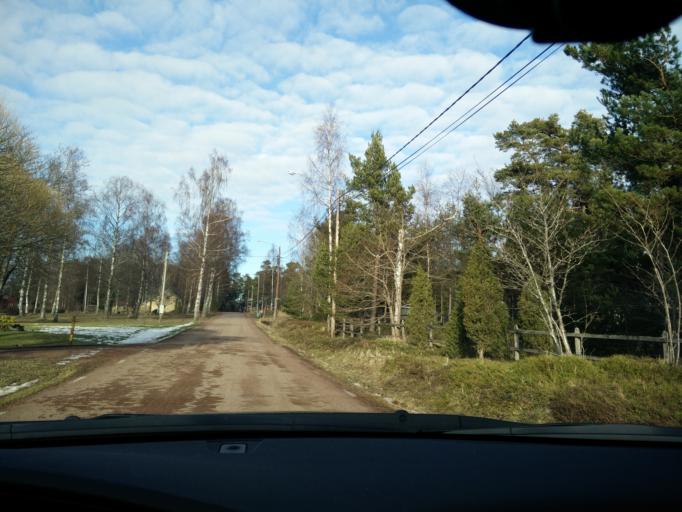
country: AX
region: Alands landsbygd
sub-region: Eckeroe
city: Eckeroe
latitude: 60.2183
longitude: 19.5495
